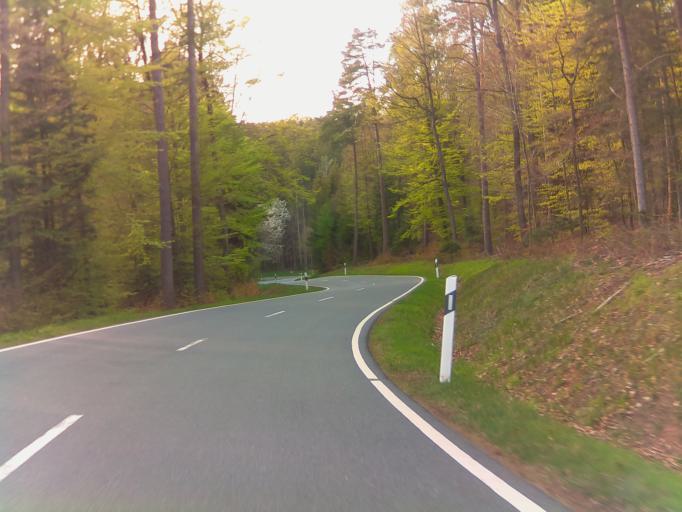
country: DE
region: Baden-Wuerttemberg
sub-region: Karlsruhe Region
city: Limbach
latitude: 49.4780
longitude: 9.1894
